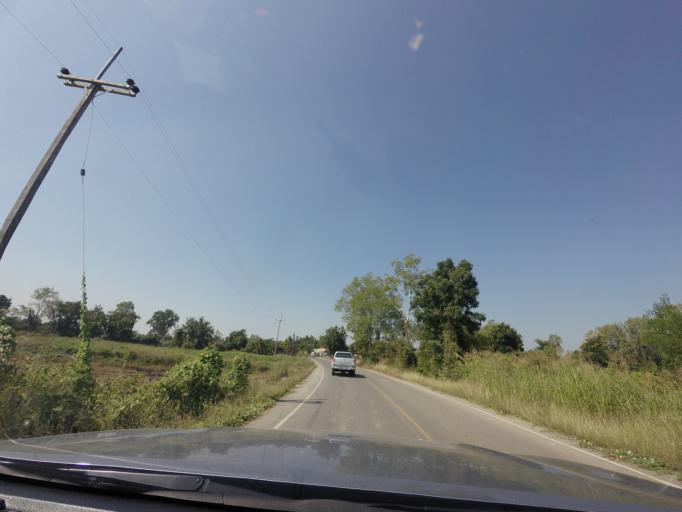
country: TH
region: Sukhothai
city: Si Samrong
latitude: 17.1310
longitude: 99.7792
